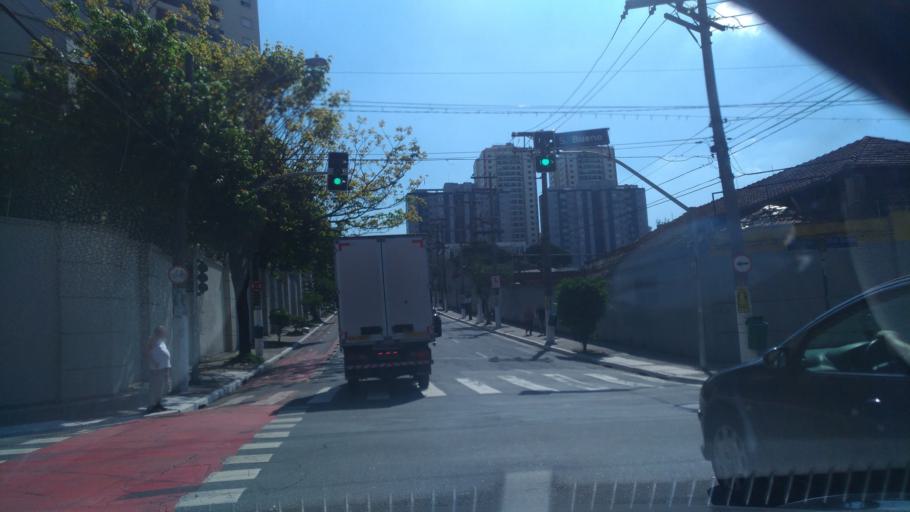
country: BR
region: Sao Paulo
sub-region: Sao Paulo
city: Sao Paulo
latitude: -23.5831
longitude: -46.6020
